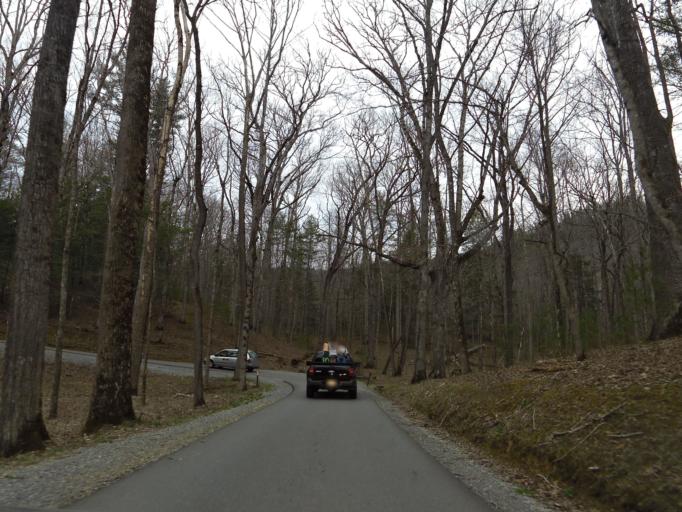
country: US
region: Tennessee
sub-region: Blount County
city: Wildwood
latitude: 35.6063
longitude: -83.8044
